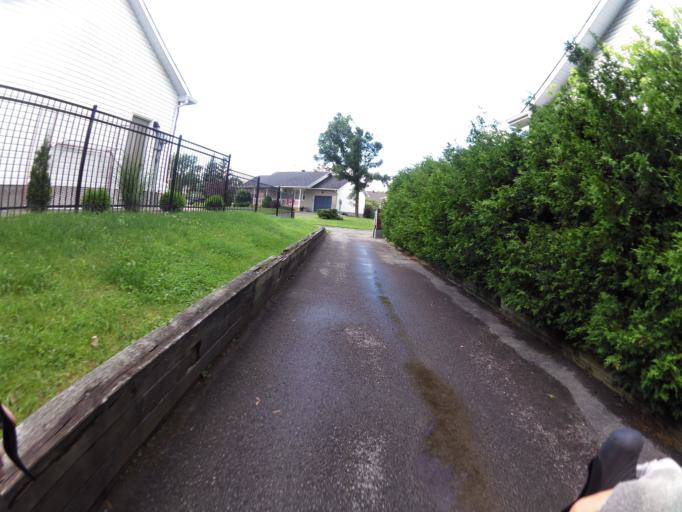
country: CA
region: Ontario
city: Bells Corners
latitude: 45.2008
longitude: -75.8356
